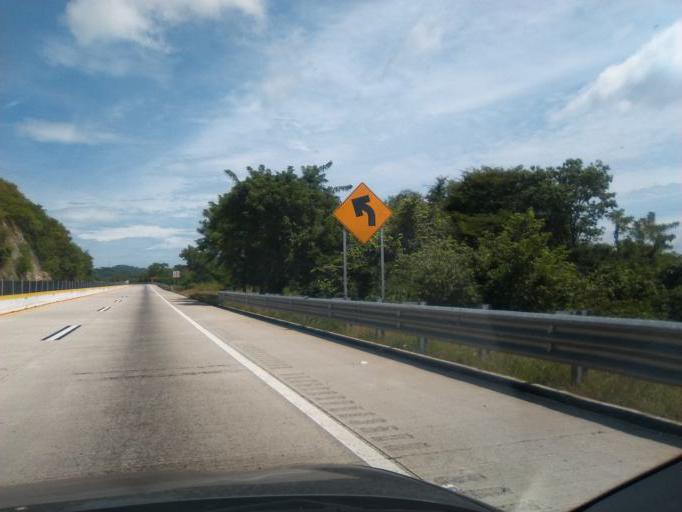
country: MX
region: Guerrero
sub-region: Acapulco de Juarez
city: Kilometro 30
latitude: 16.9438
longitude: -99.7690
